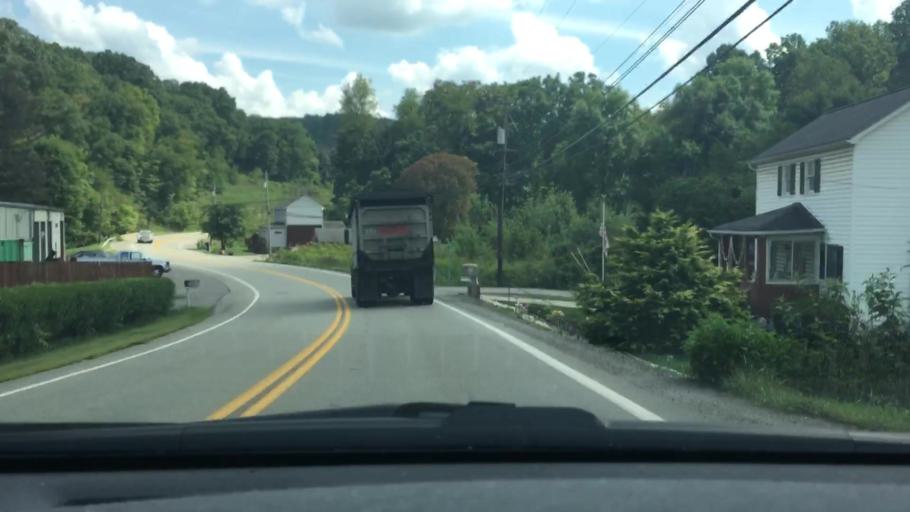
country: US
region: Pennsylvania
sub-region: Washington County
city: Gastonville
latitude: 40.2554
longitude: -79.9880
